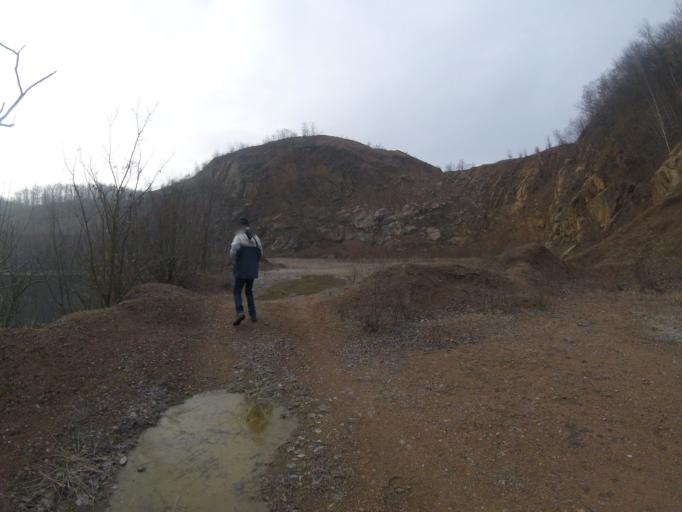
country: HU
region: Baranya
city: Mecseknadasd
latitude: 46.1485
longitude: 18.5191
